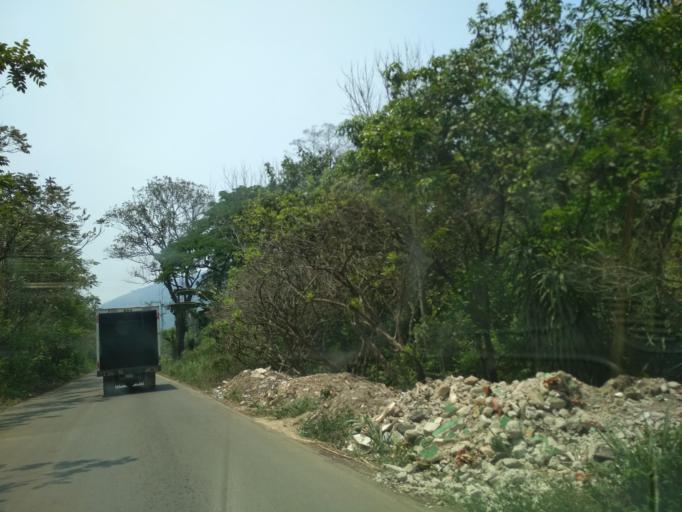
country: MX
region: Veracruz
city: Tezonapa
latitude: 18.6091
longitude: -96.6925
